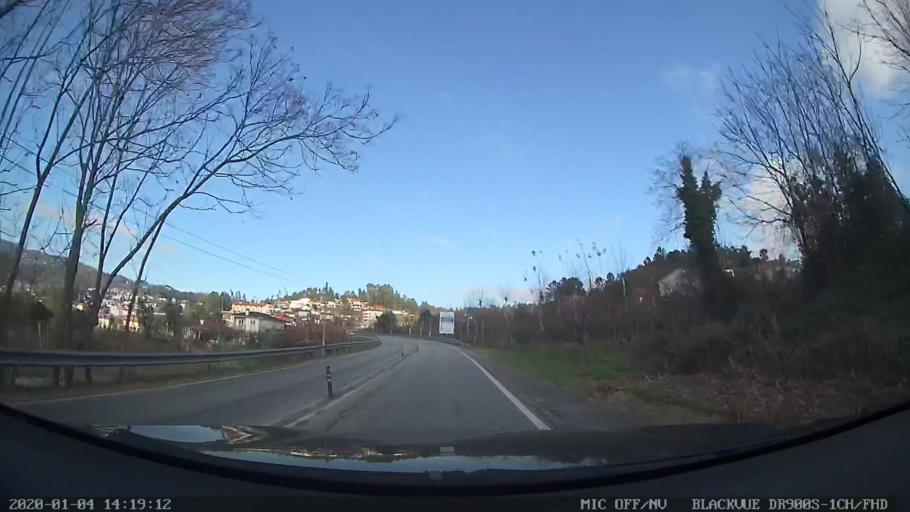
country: PT
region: Braga
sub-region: Celorico de Basto
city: Celorico de Basto
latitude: 41.3856
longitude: -7.9954
